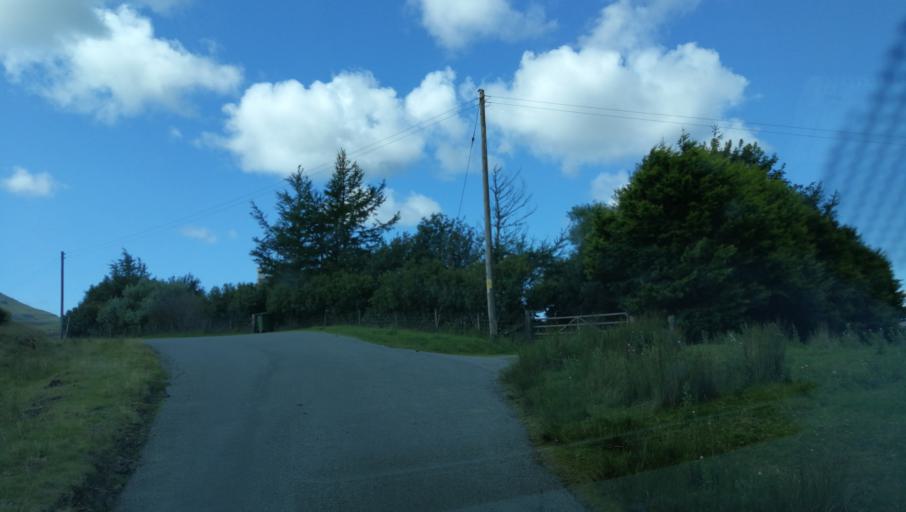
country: GB
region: Scotland
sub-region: Highland
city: Isle of Skye
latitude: 57.4277
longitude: -6.5793
